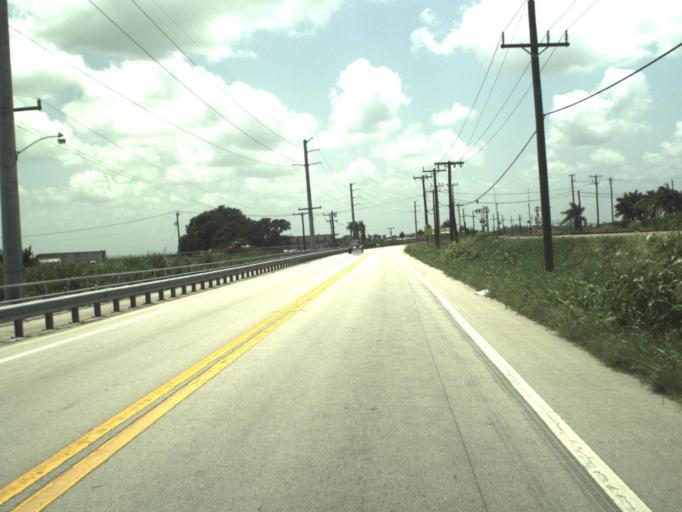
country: US
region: Florida
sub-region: Palm Beach County
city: Pahokee
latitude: 26.8293
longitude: -80.6449
